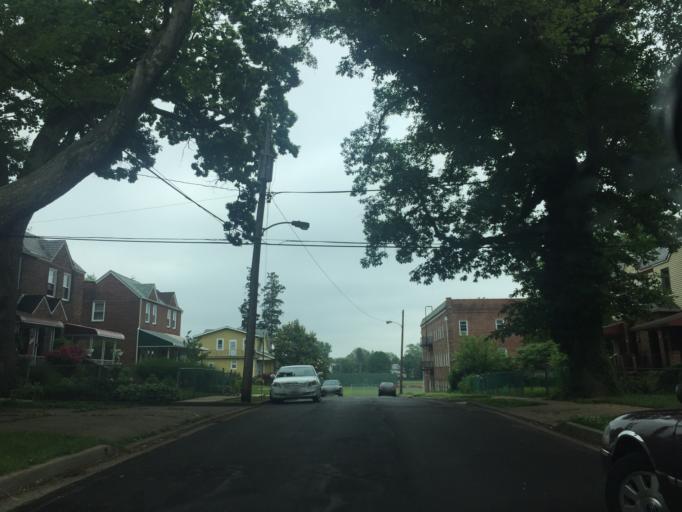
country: US
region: Maryland
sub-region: Baltimore County
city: Lochearn
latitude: 39.3321
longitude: -76.6917
